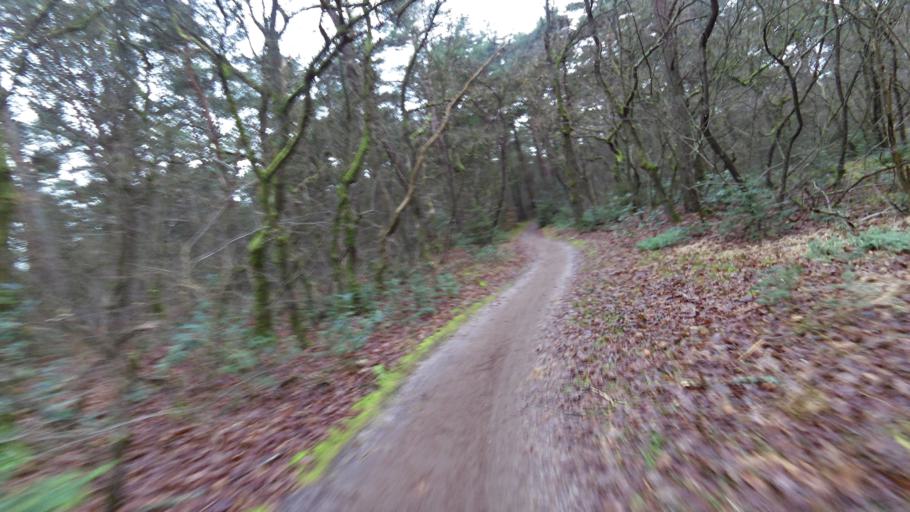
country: NL
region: North Holland
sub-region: Gemeente Bergen
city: Egmond aan Zee
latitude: 52.6859
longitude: 4.6760
